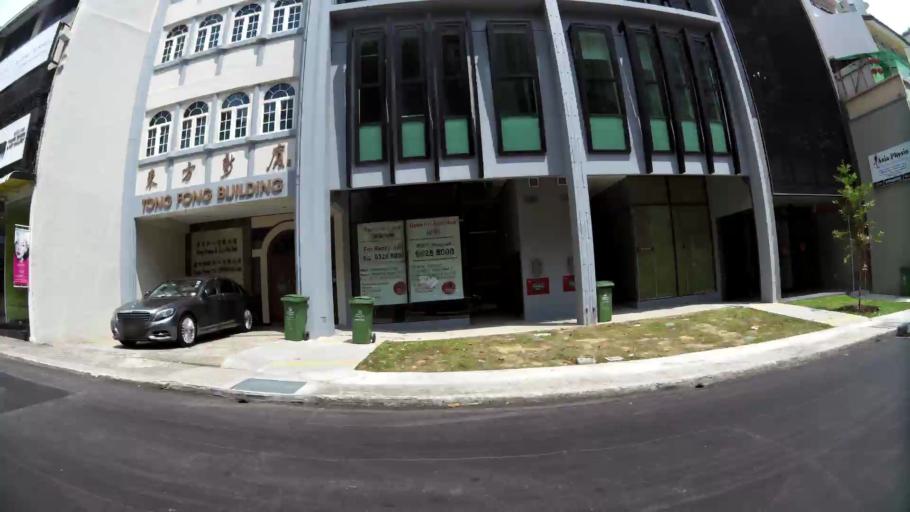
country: SG
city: Singapore
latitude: 1.2951
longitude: 103.8417
